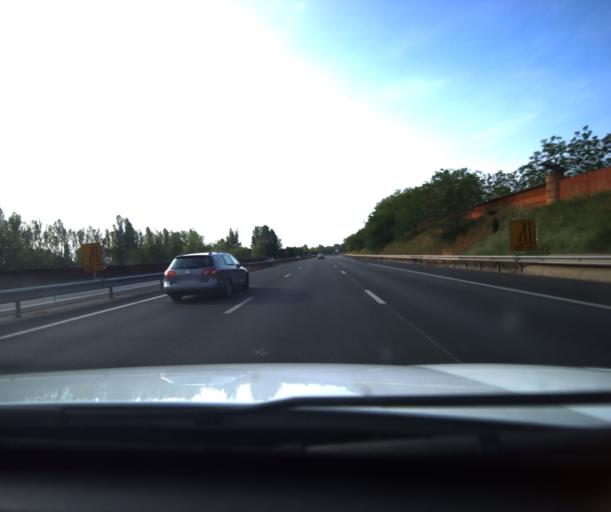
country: FR
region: Midi-Pyrenees
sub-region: Departement de la Haute-Garonne
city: Aucamville
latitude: 43.6709
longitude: 1.4187
